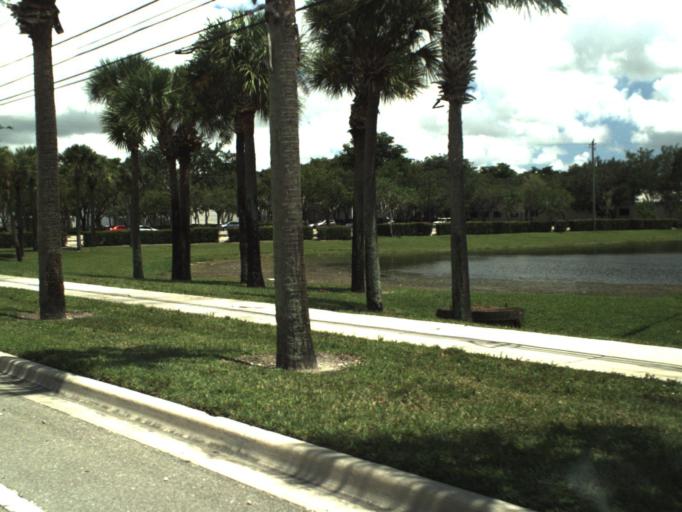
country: US
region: Florida
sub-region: Miami-Dade County
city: Country Club
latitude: 25.9803
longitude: -80.2854
